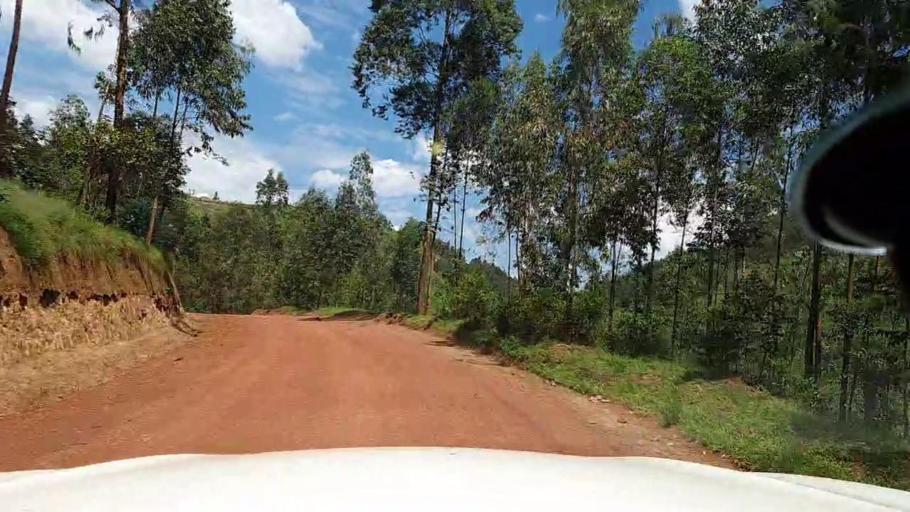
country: RW
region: Northern Province
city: Byumba
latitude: -1.7439
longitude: 29.8630
